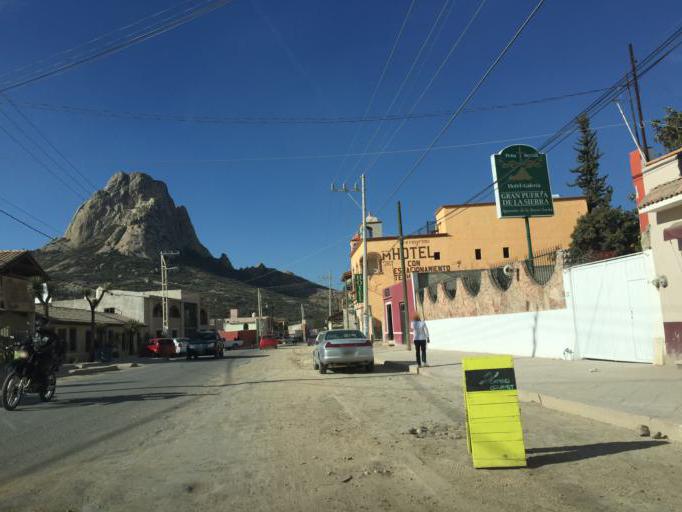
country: MX
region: Queretaro
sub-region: Ezequiel Montes
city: San Jose del Jagueey
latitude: 20.7393
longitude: -99.9387
